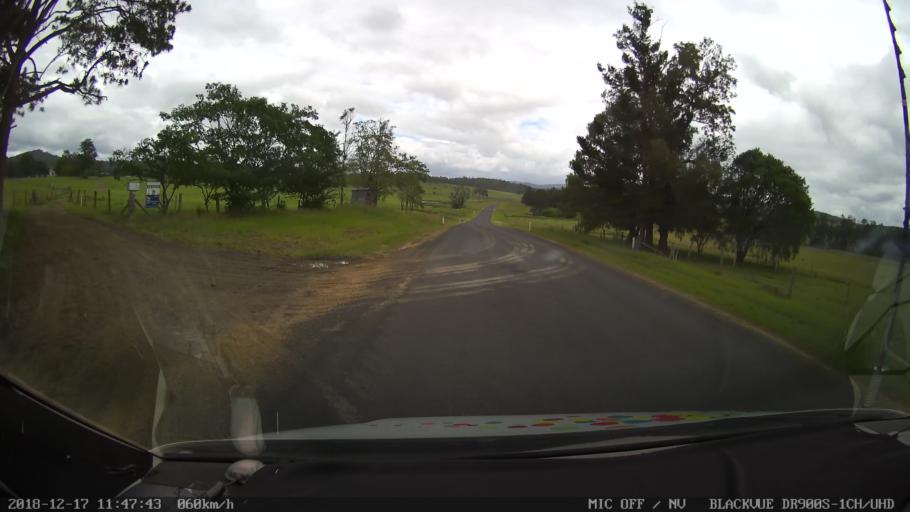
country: AU
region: New South Wales
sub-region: Kyogle
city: Kyogle
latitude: -28.6246
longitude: 152.5910
